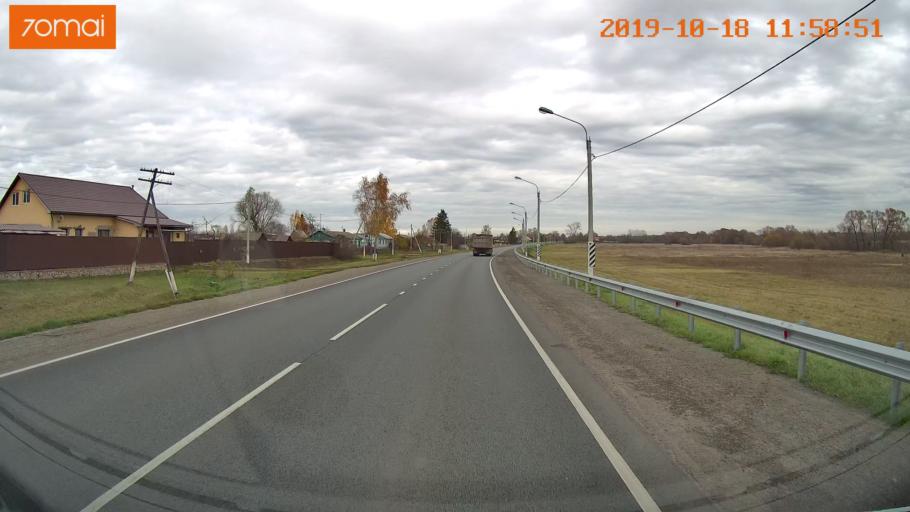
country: RU
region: Rjazan
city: Zakharovo
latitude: 54.2760
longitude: 39.1702
